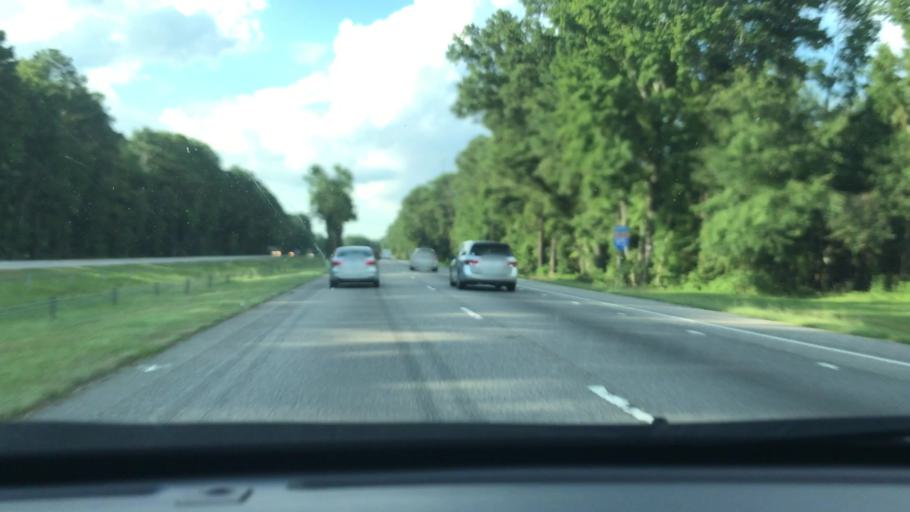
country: US
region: North Carolina
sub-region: Robeson County
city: Saint Pauls
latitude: 34.8170
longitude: -78.9846
